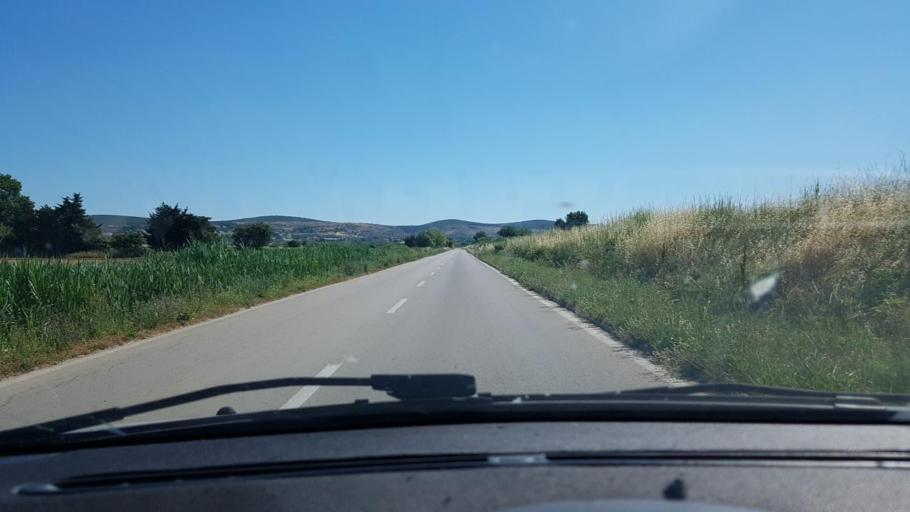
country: HR
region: Zadarska
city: Pakostane
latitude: 43.9432
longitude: 15.5240
